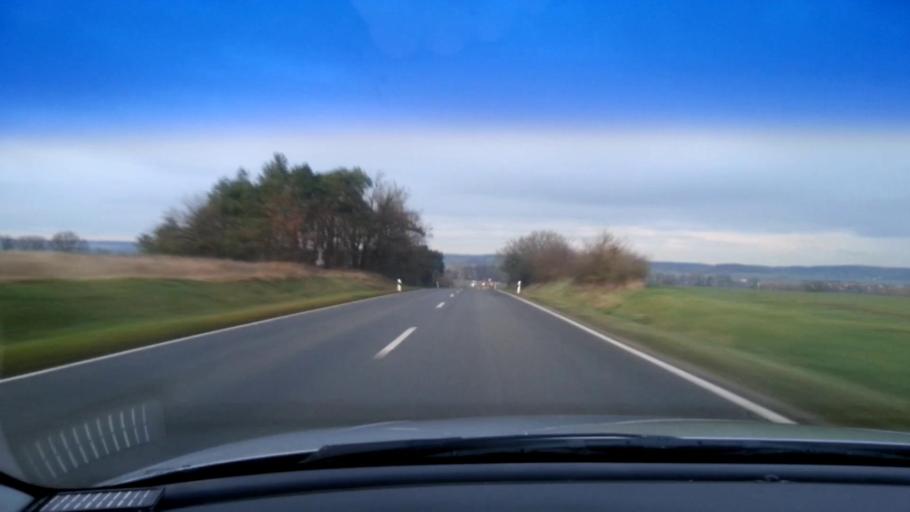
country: DE
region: Bavaria
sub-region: Upper Franconia
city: Frensdorf
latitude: 49.8158
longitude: 10.8403
